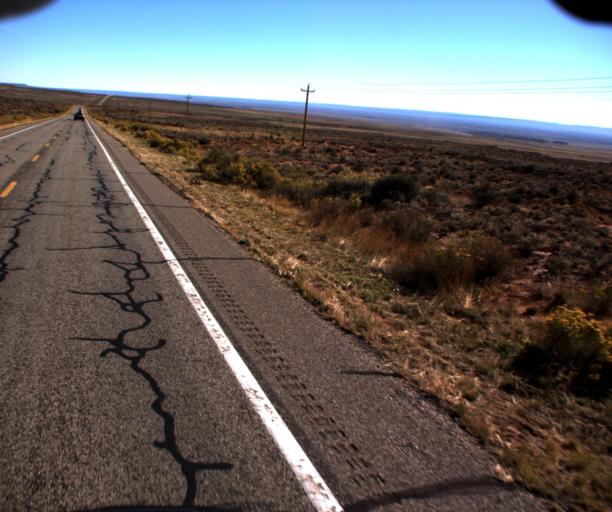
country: US
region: Arizona
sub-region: Coconino County
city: Fredonia
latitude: 36.8602
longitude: -112.7195
